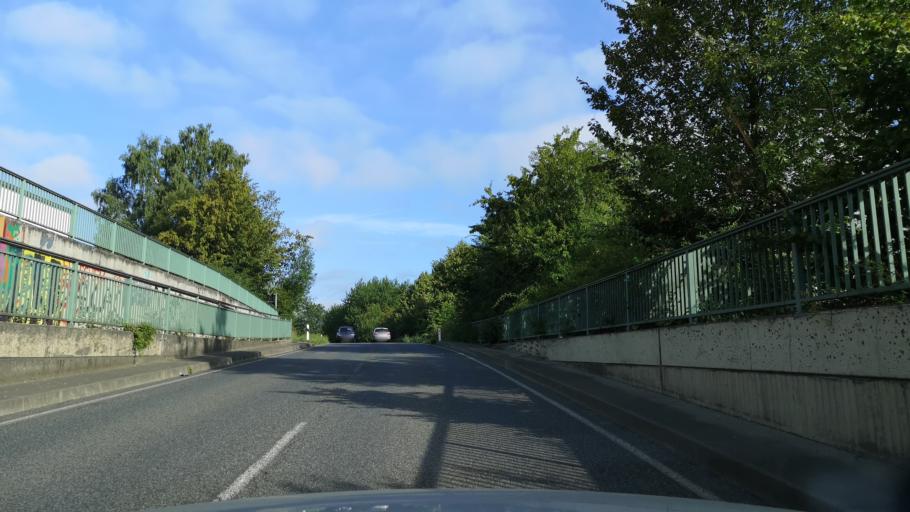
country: DE
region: North Rhine-Westphalia
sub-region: Regierungsbezirk Dusseldorf
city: Wuppertal
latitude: 51.3068
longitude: 7.1164
